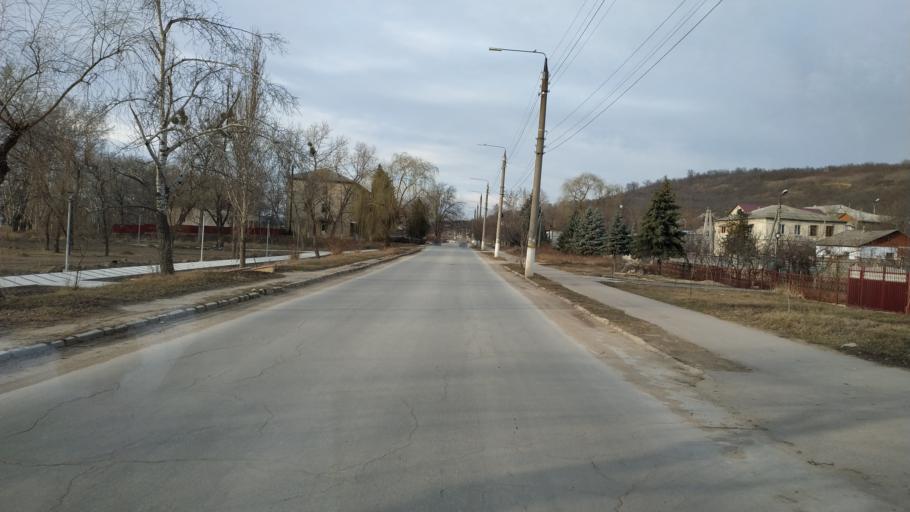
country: MD
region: Nisporeni
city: Nisporeni
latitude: 47.0841
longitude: 28.1825
